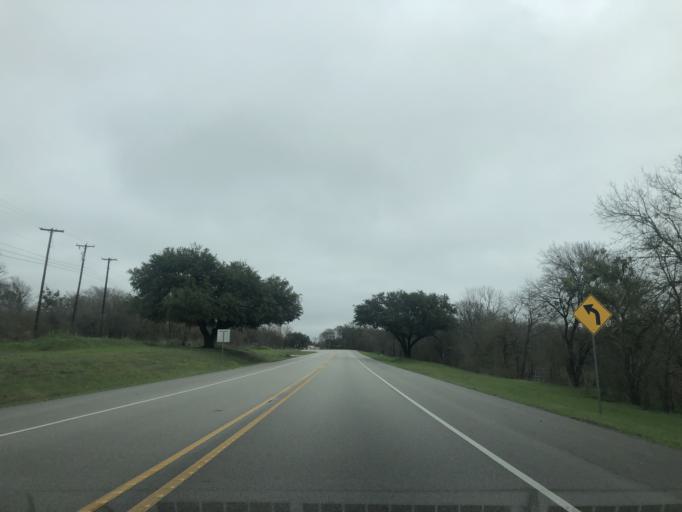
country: US
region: Texas
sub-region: Williamson County
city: Hutto
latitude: 30.6390
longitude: -97.5694
